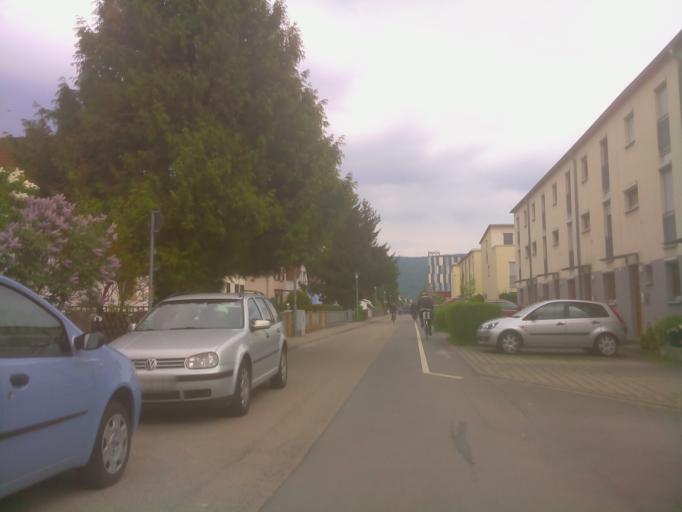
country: DE
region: Baden-Wuerttemberg
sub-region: Karlsruhe Region
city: Eppelheim
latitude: 49.4098
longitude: 8.6564
